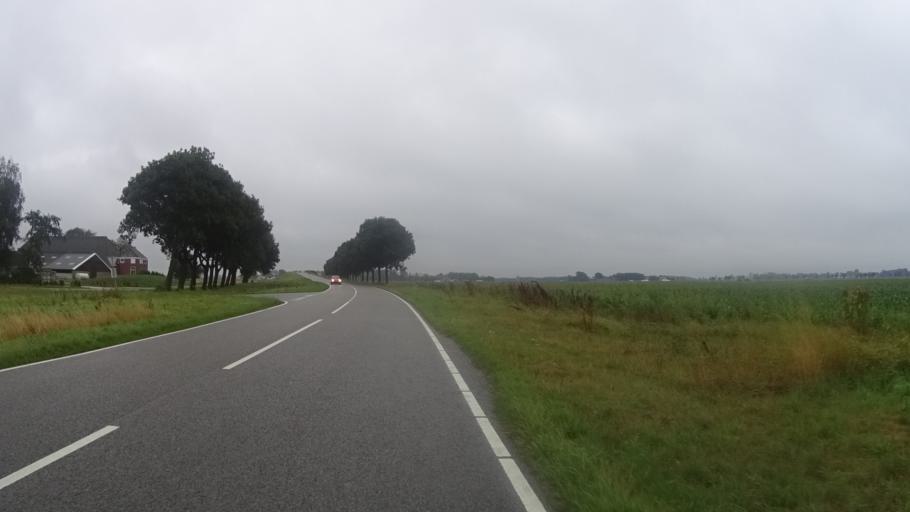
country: NL
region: Groningen
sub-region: Gemeente Veendam
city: Veendam
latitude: 53.1877
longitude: 6.9388
